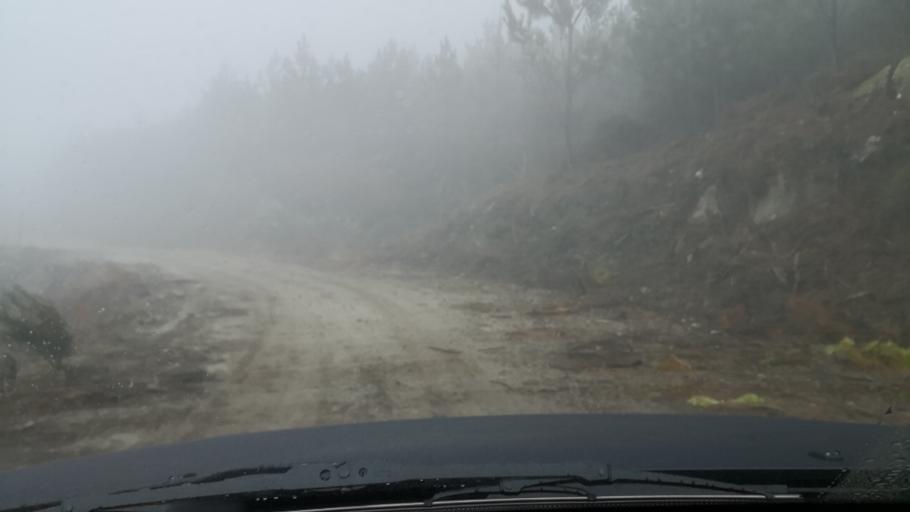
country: PT
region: Vila Real
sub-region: Vila Real
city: Vila Real
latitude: 41.3704
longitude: -7.7461
